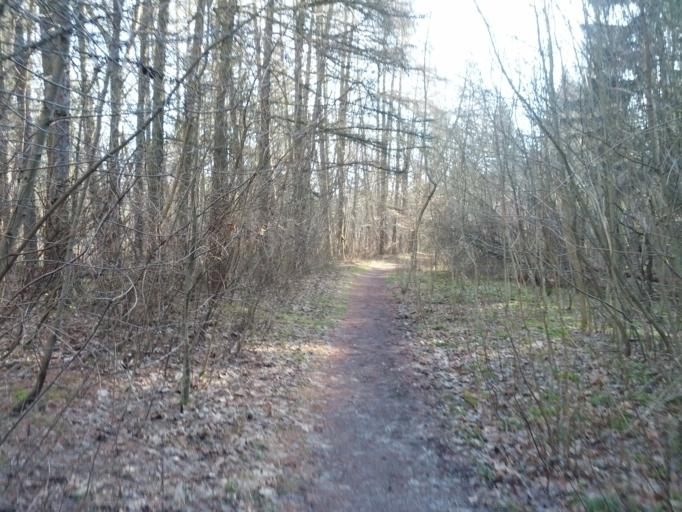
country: DE
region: Thuringia
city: Weberstedt
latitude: 51.0919
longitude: 10.5126
